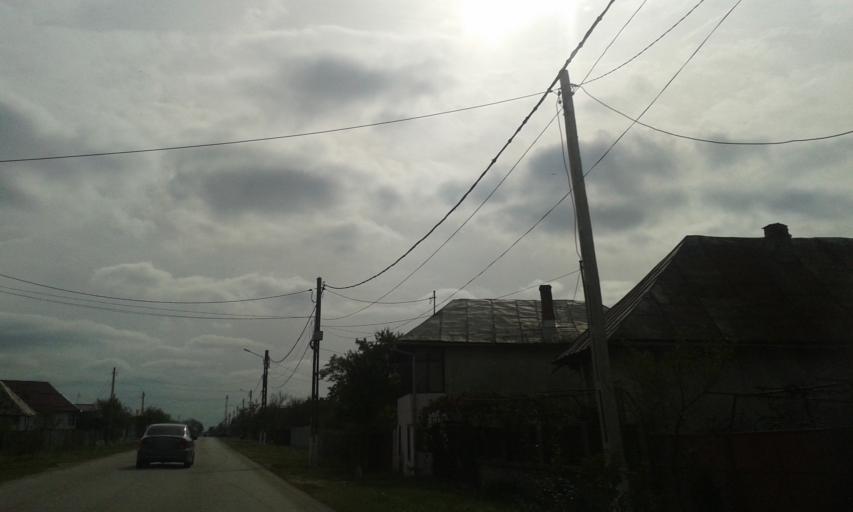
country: RO
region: Gorj
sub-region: Comuna Targu Carbunesti
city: Pojogeni
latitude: 44.9985
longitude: 23.4923
